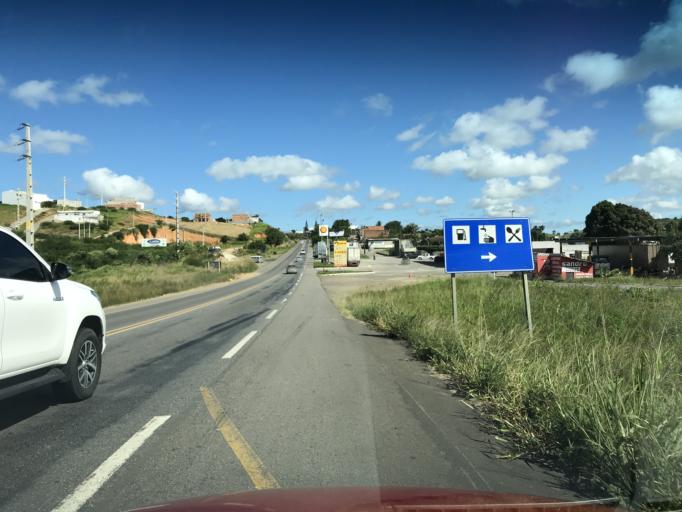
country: BR
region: Bahia
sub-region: Santo Antonio De Jesus
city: Santo Antonio de Jesus
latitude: -12.9559
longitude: -39.2630
